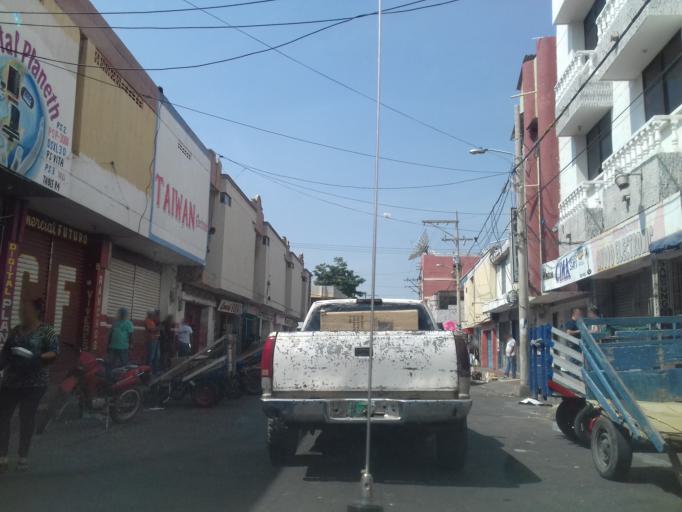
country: CO
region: La Guajira
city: Maicao
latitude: 11.3785
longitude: -72.2385
